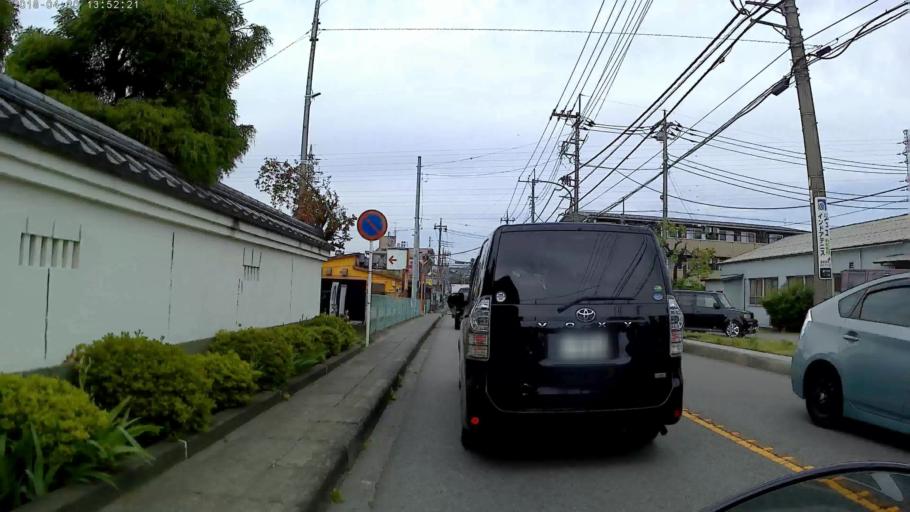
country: JP
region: Tokyo
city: Hachioji
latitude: 35.5922
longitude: 139.3732
